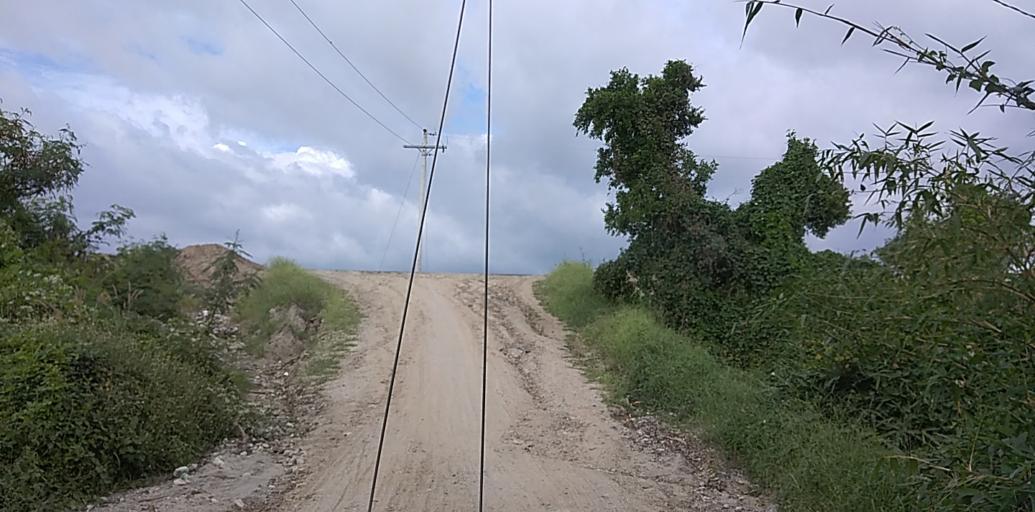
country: PH
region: Central Luzon
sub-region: Province of Pampanga
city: Pulung Santol
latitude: 15.0592
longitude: 120.5663
